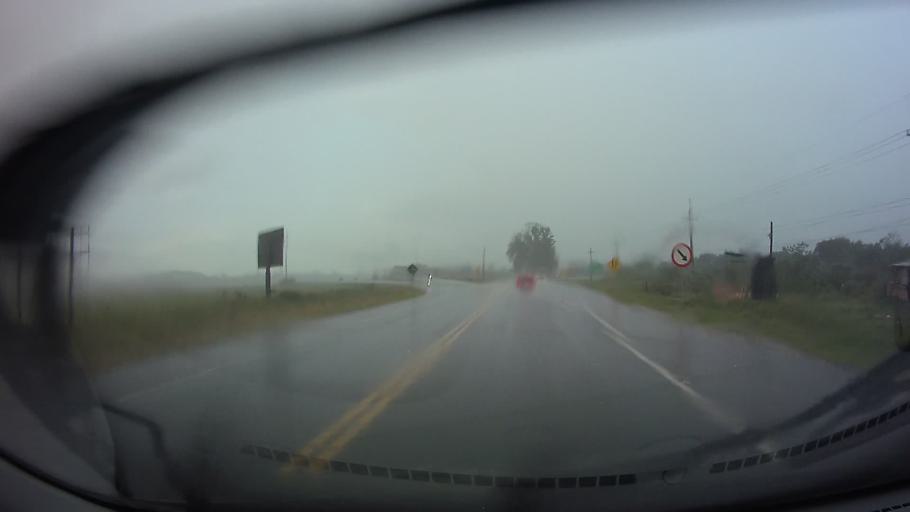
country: PY
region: Paraguari
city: Paraguari
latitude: -25.6385
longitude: -57.1548
